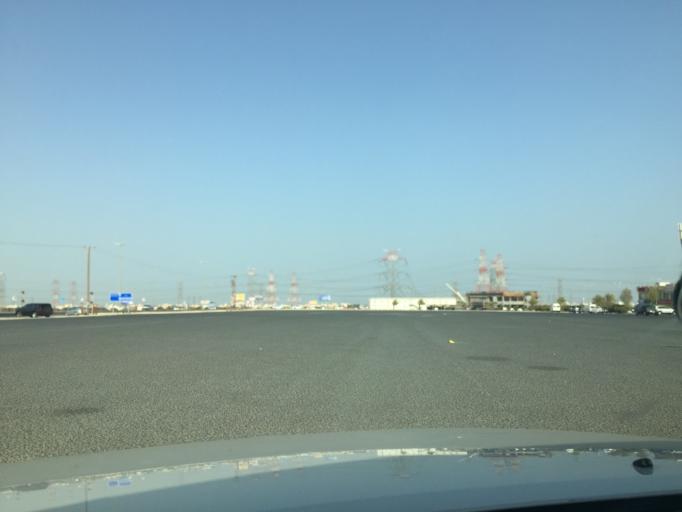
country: KW
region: Mubarak al Kabir
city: Mubarak al Kabir
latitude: 29.2031
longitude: 48.0490
